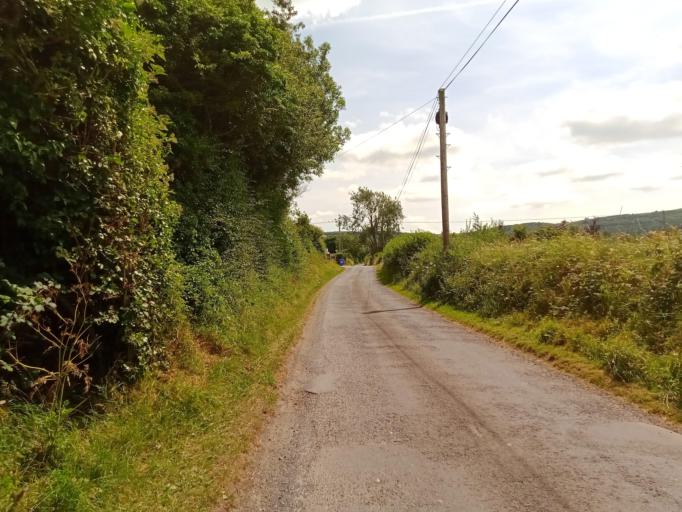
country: IE
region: Leinster
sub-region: Laois
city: Rathdowney
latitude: 52.8150
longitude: -7.4720
